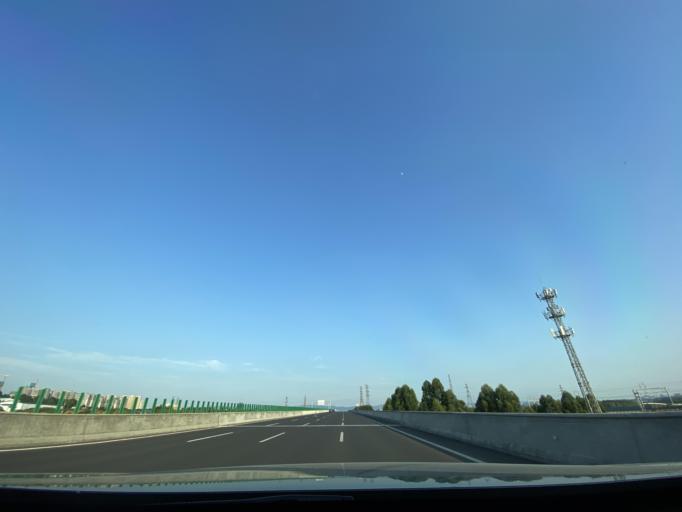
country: CN
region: Sichuan
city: Chengdu
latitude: 30.5946
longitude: 104.1194
